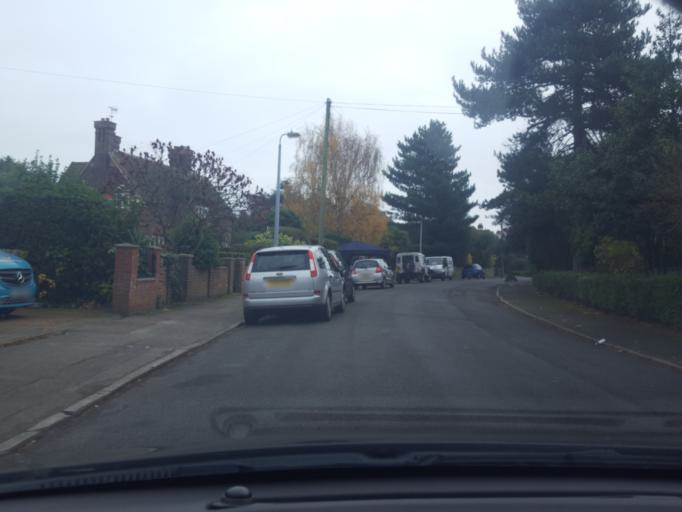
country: GB
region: England
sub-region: Essex
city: Clacton-on-Sea
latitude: 51.7967
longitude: 1.1689
